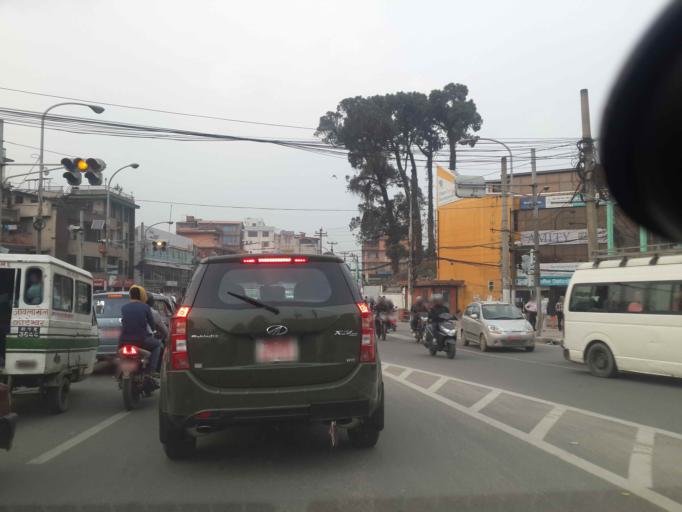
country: NP
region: Central Region
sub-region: Bagmati Zone
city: Kathmandu
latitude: 27.6905
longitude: 85.3176
